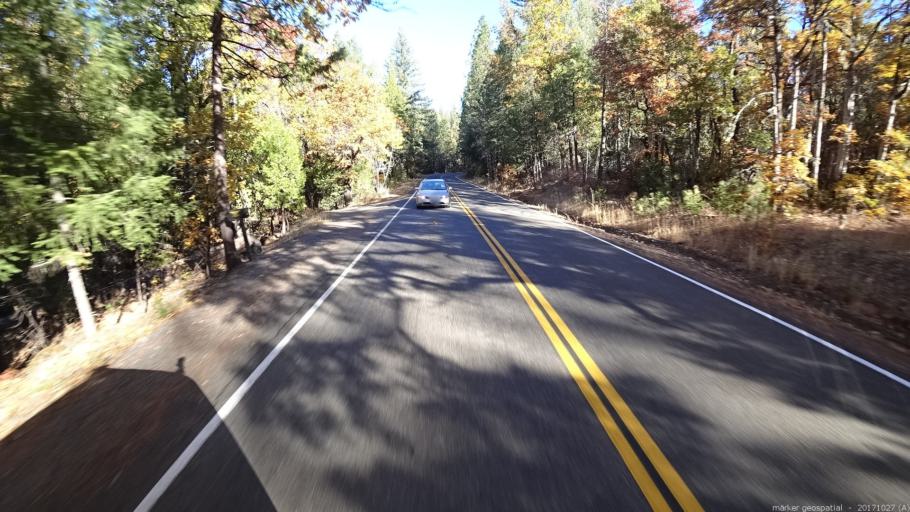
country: US
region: California
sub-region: Shasta County
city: Burney
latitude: 40.9118
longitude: -121.9082
